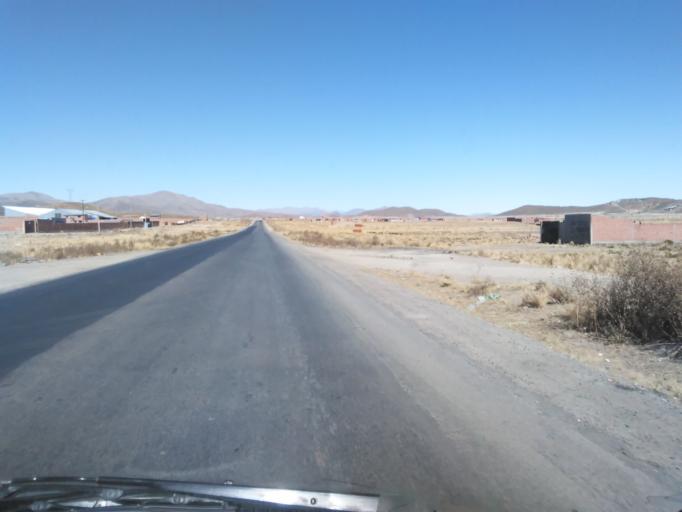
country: BO
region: Oruro
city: Oruro
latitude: -17.9996
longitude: -67.0435
